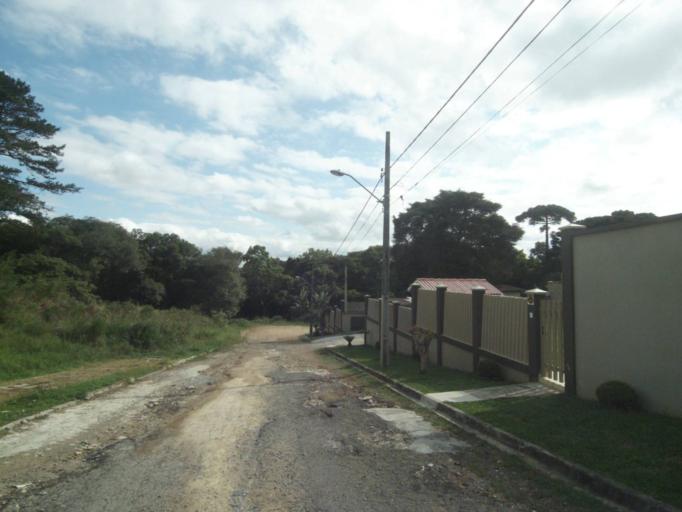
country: BR
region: Parana
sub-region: Curitiba
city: Curitiba
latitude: -25.3820
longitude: -49.2976
